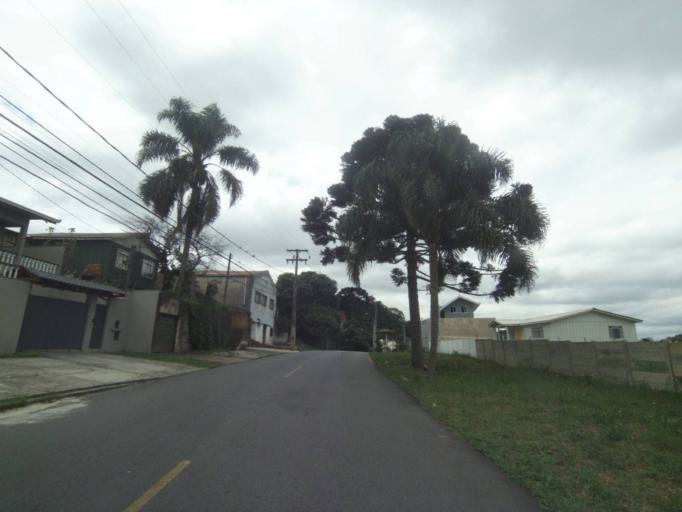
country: BR
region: Parana
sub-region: Curitiba
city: Curitiba
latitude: -25.3982
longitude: -49.2809
